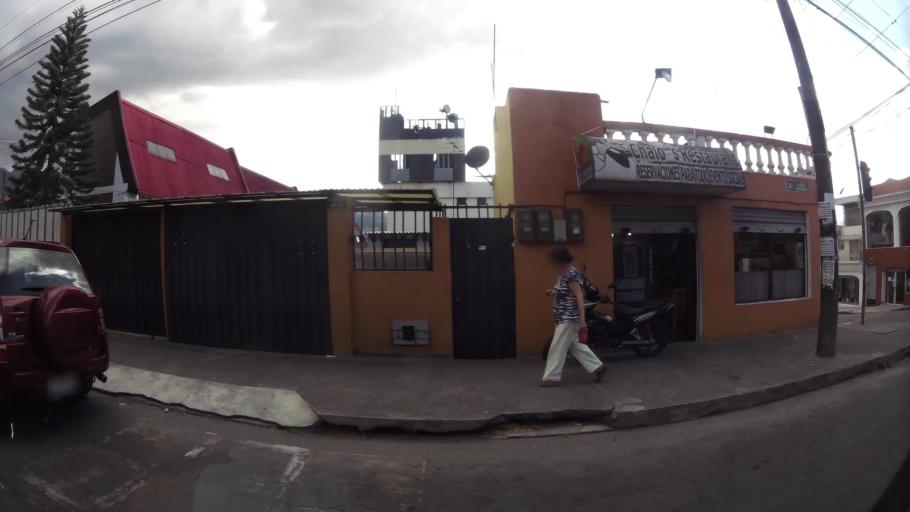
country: EC
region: Pichincha
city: Quito
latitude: -0.1233
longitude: -78.4855
